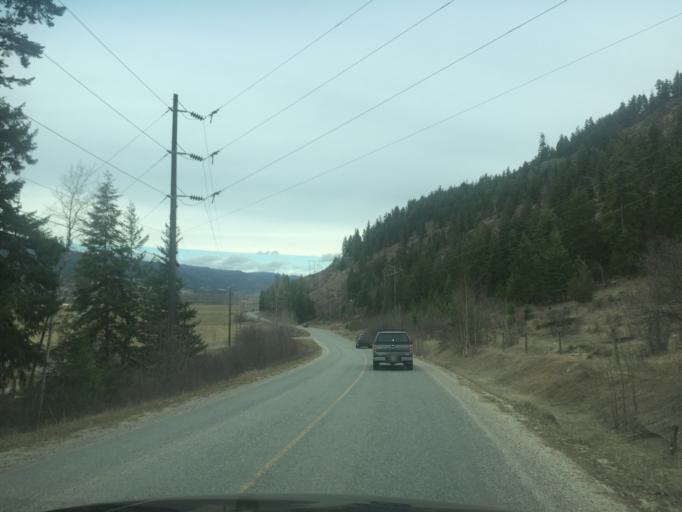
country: CA
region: British Columbia
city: Kamloops
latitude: 51.2021
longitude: -120.1361
